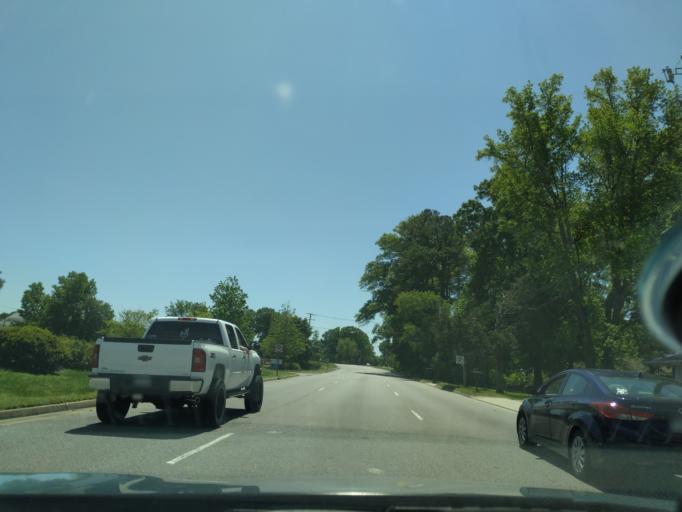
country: US
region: Virginia
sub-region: Prince George County
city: Fort Lee
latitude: 37.2730
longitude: -77.3165
